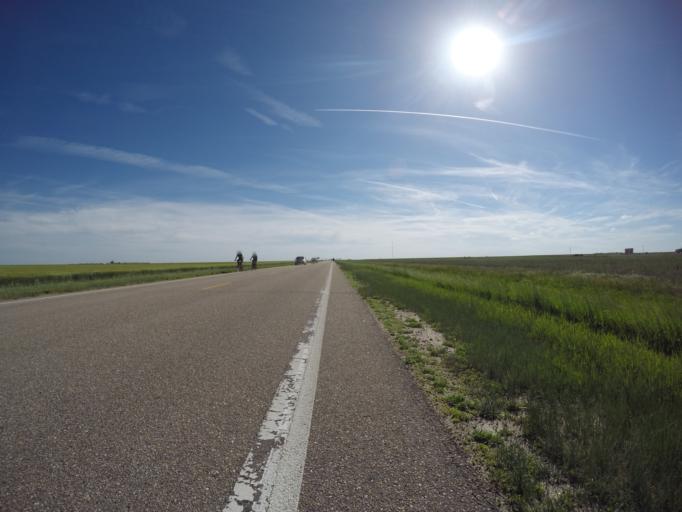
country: US
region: Kansas
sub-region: Cheyenne County
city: Saint Francis
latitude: 39.7539
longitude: -102.0454
